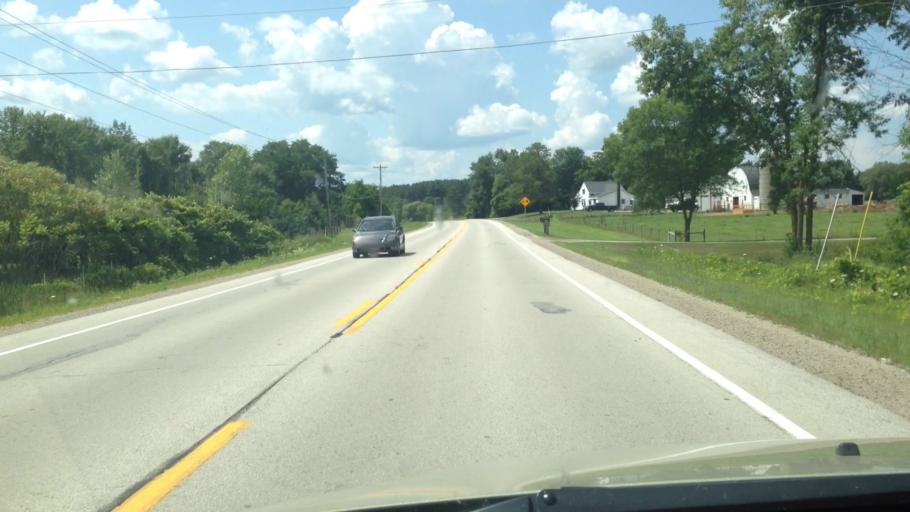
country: US
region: Wisconsin
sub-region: Brown County
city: Suamico
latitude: 44.6457
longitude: -88.0961
